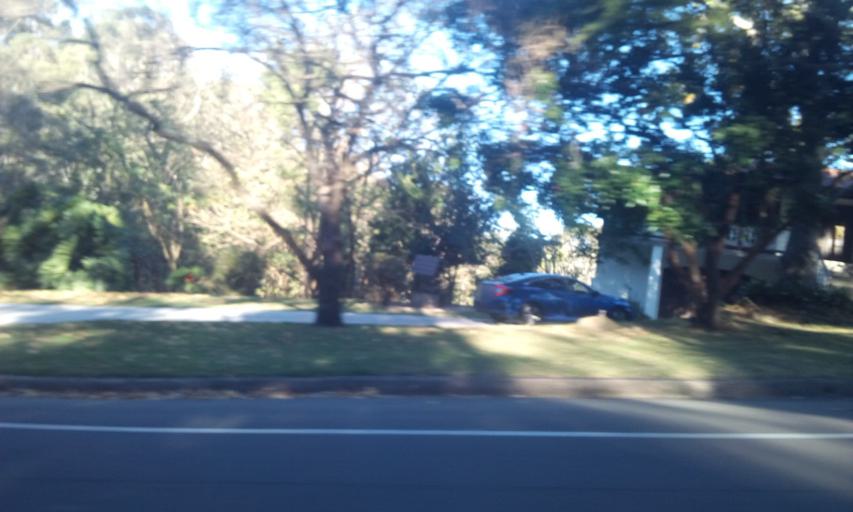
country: AU
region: New South Wales
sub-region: Wollongong
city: Mount Keira
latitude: -34.4244
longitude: 150.8479
